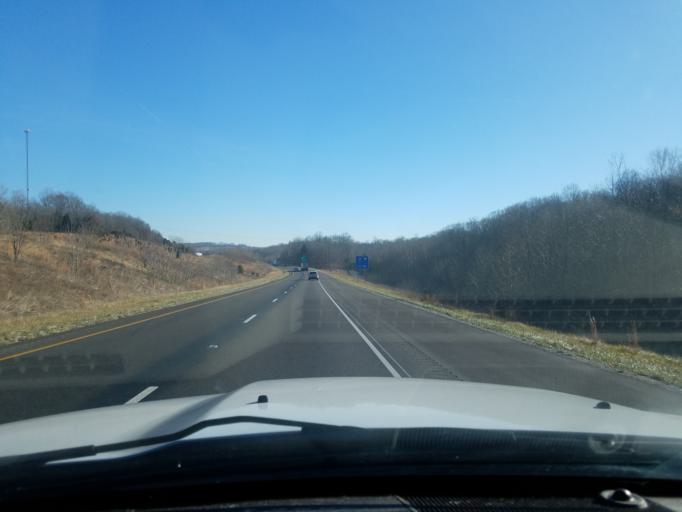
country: US
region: Indiana
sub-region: Crawford County
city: English
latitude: 38.2380
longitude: -86.4801
